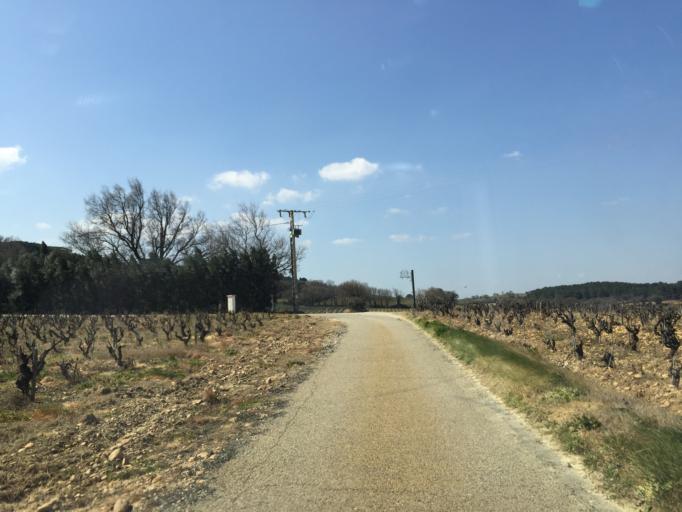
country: FR
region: Provence-Alpes-Cote d'Azur
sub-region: Departement du Vaucluse
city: Courthezon
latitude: 44.0609
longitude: 4.8763
